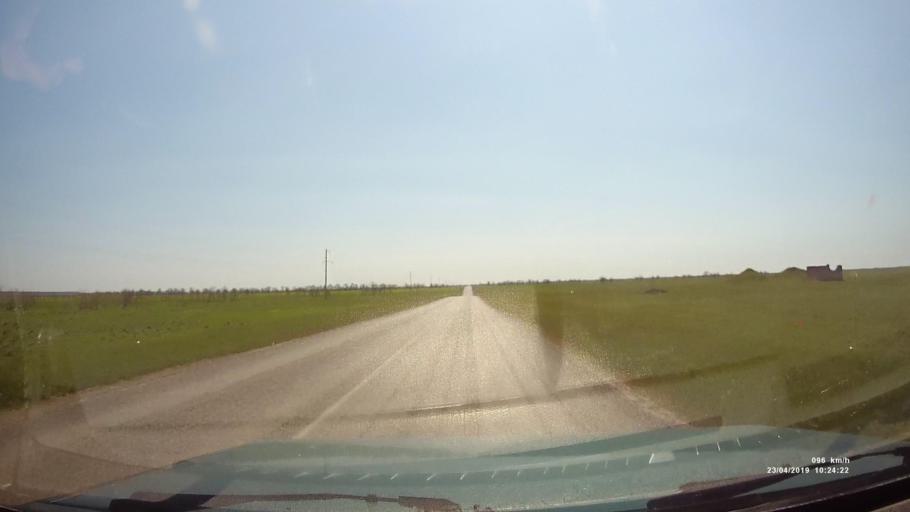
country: RU
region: Rostov
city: Sovetskoye
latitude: 46.6394
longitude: 42.4405
